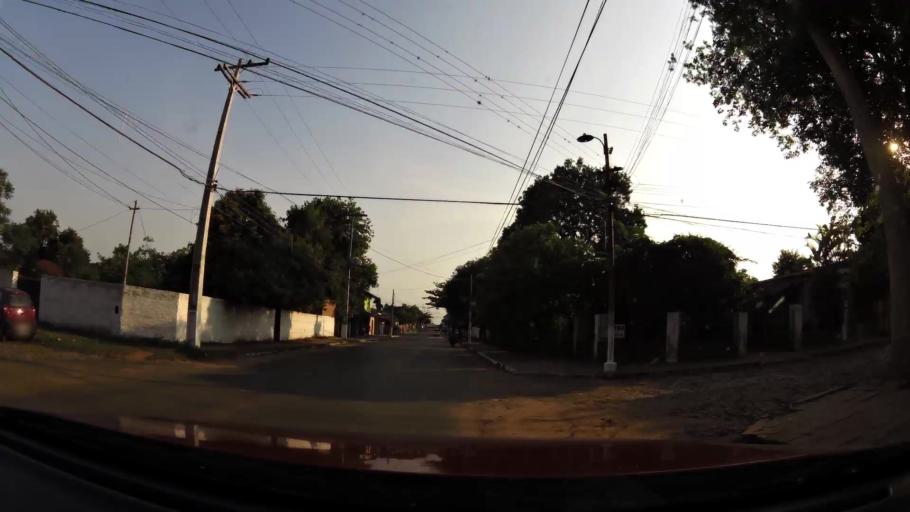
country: PY
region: Central
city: Lambare
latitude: -25.3550
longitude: -57.5975
